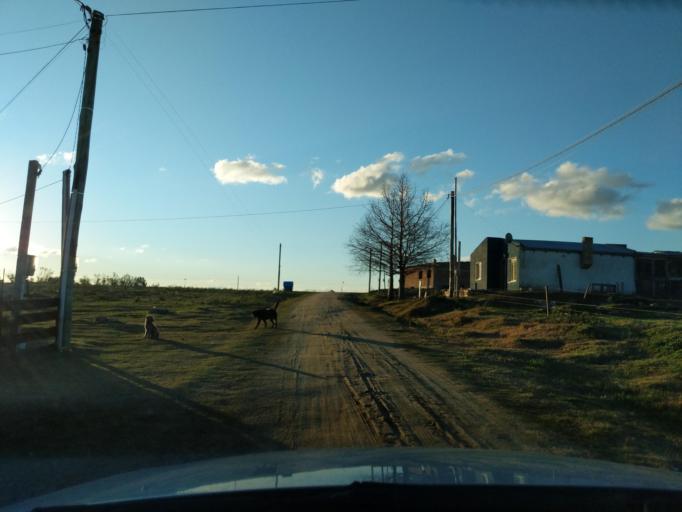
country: UY
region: Florida
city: Florida
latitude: -34.1037
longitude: -56.2386
